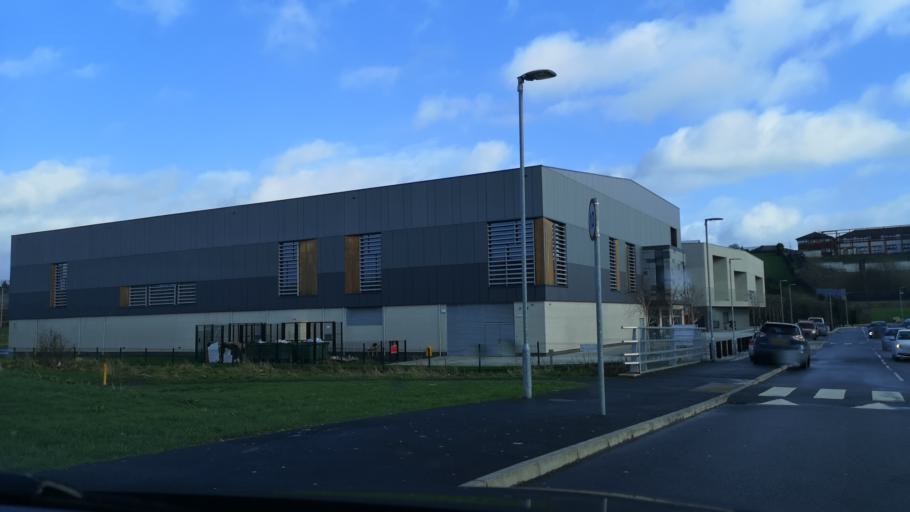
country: GB
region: Northern Ireland
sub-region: Newry and Mourne District
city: Newry
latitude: 54.1802
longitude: -6.3464
